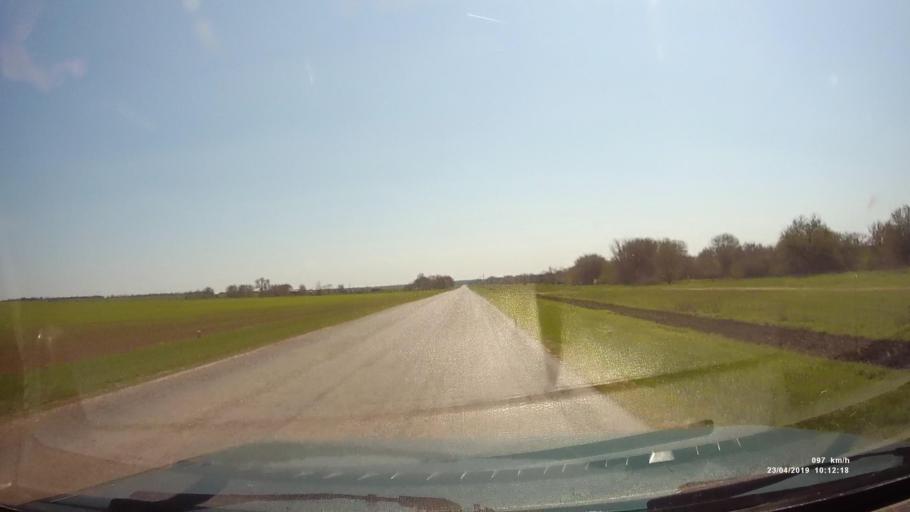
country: RU
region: Rostov
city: Sovetskoye
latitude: 46.6907
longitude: 42.3340
